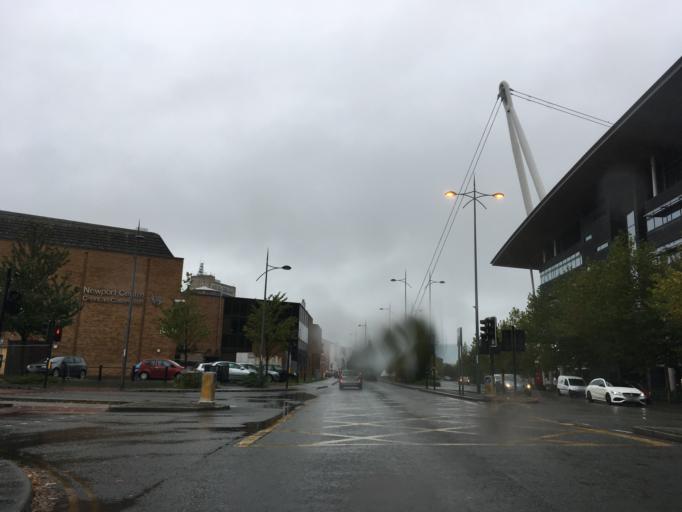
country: GB
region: Wales
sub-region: Newport
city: Newport
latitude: 51.5853
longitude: -2.9900
